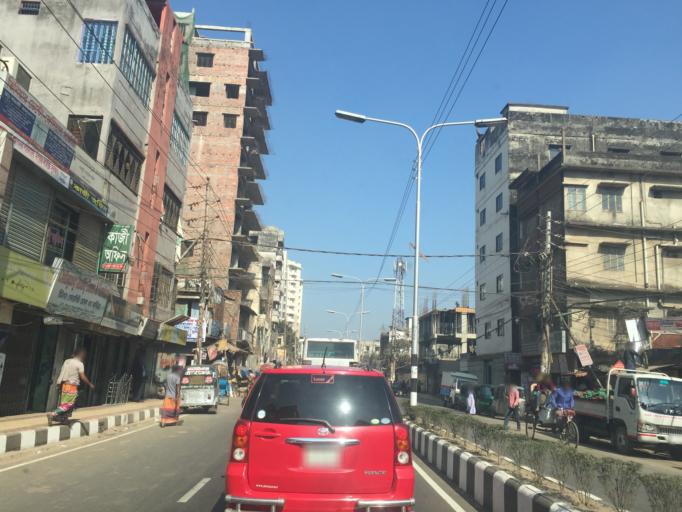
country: BD
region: Dhaka
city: Azimpur
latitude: 23.7880
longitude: 90.3479
